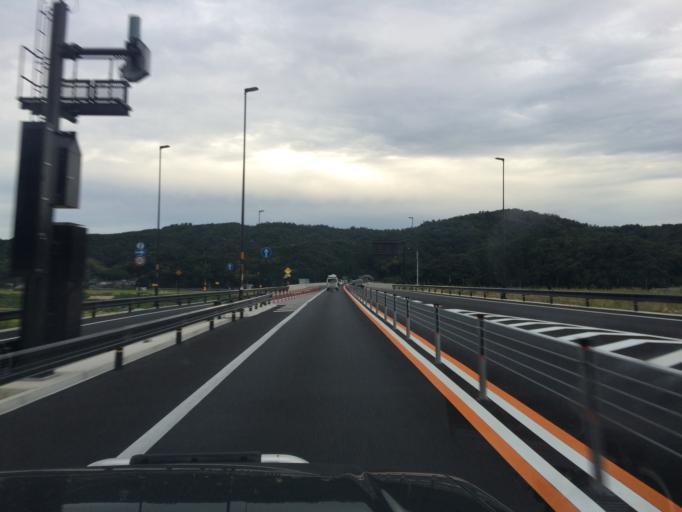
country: JP
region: Tottori
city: Tottori
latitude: 35.5014
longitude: 134.0732
